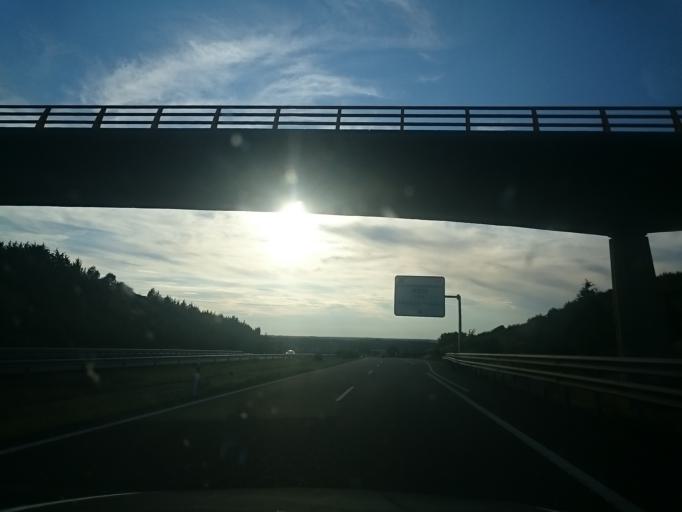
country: ES
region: Castille and Leon
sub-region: Provincia de Leon
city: Sahagun
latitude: 42.3824
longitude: -5.0214
